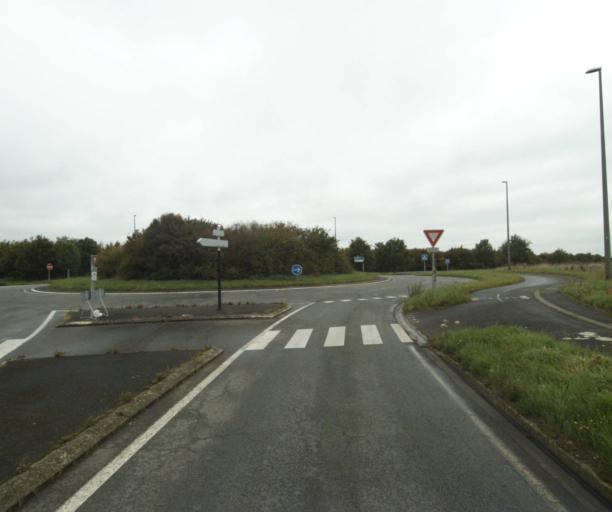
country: FR
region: Nord-Pas-de-Calais
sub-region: Departement du Nord
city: Wavrin
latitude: 50.5890
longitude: 2.9286
